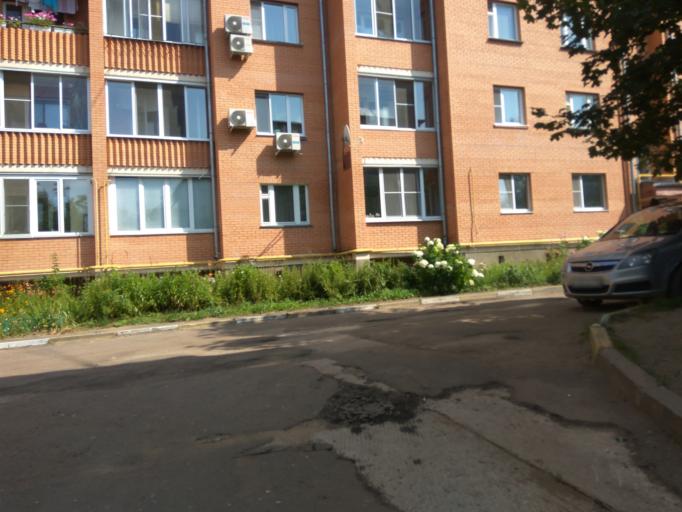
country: RU
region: Moskovskaya
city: Kubinka
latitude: 55.5804
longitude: 36.7673
